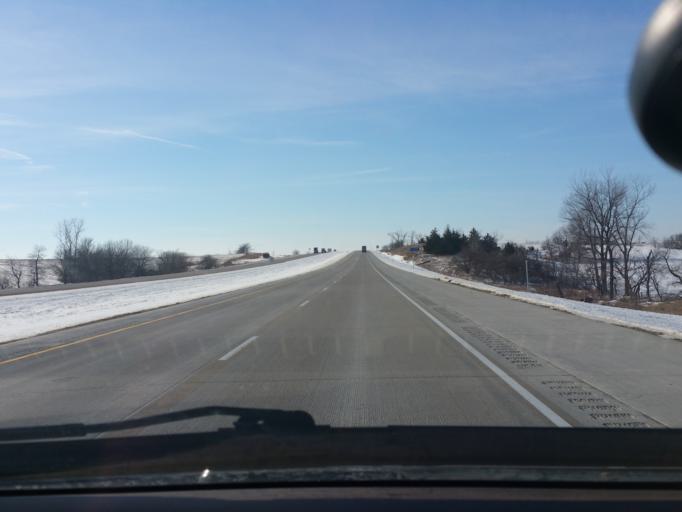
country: US
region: Iowa
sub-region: Decatur County
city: Lamoni
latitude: 40.5817
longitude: -93.9308
